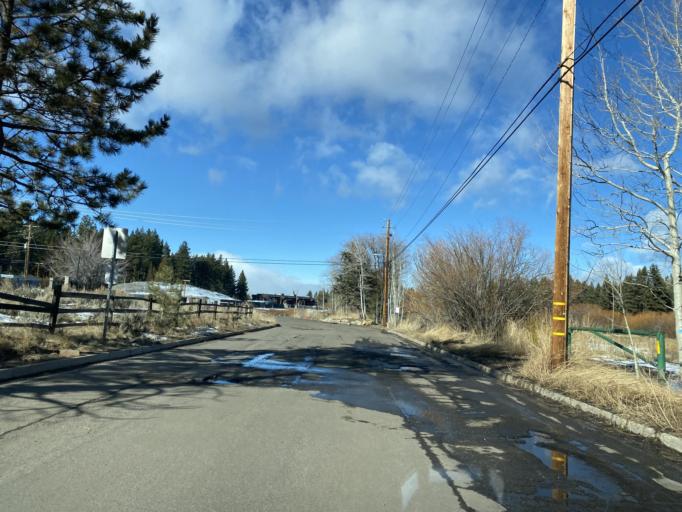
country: US
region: Nevada
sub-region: Douglas County
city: Kingsbury
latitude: 38.9731
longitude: -119.9418
